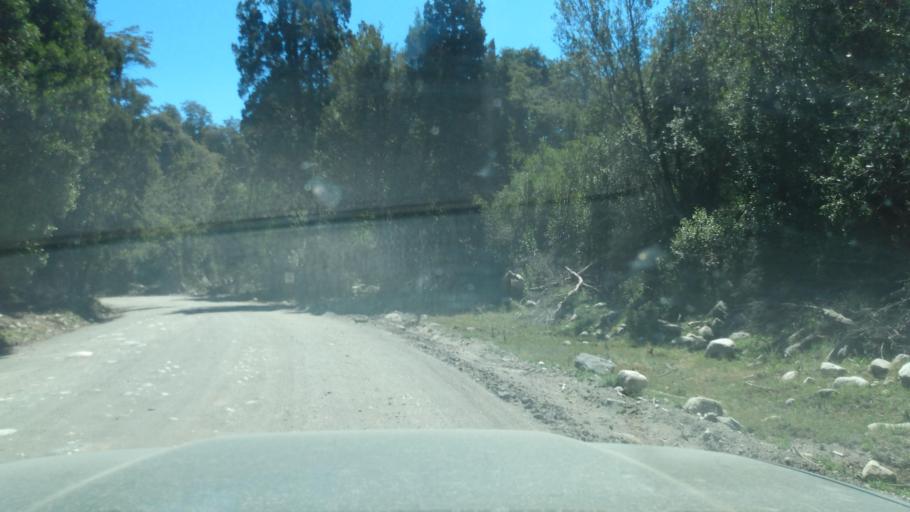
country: AR
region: Neuquen
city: Villa La Angostura
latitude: -40.6224
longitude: -71.5146
